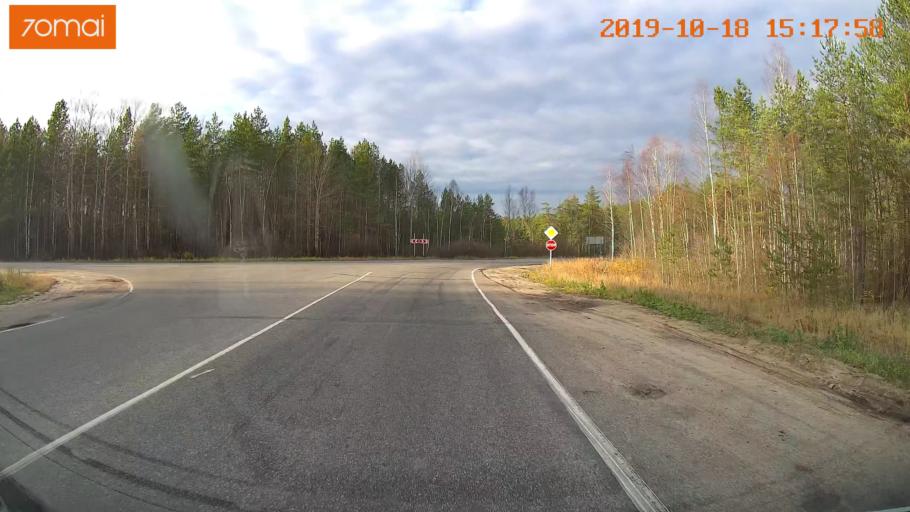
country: RU
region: Vladimir
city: Anopino
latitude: 55.6568
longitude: 40.7270
